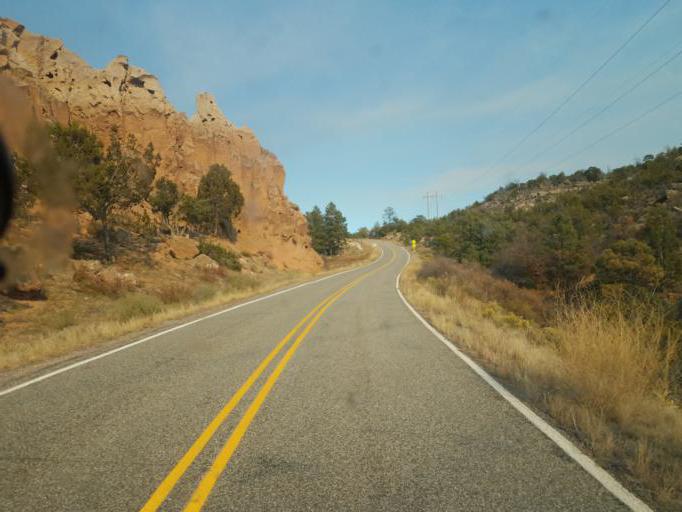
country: US
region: New Mexico
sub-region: Los Alamos County
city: White Rock
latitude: 35.8108
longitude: -106.2465
